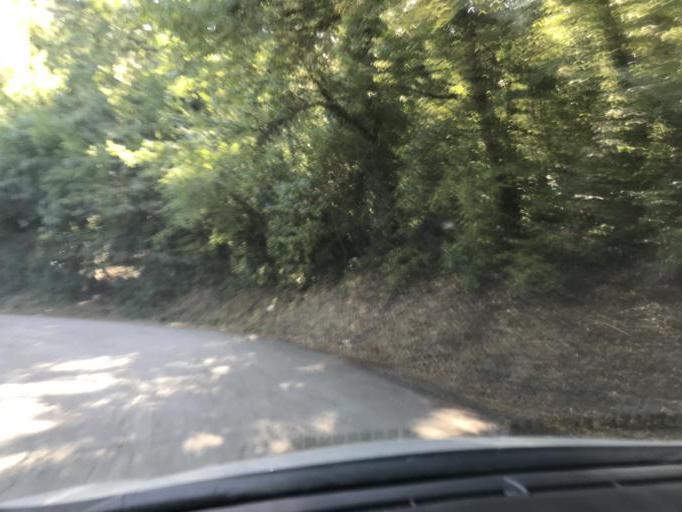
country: IT
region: Umbria
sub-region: Provincia di Terni
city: Avigliano Umbro
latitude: 42.6157
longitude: 12.4084
